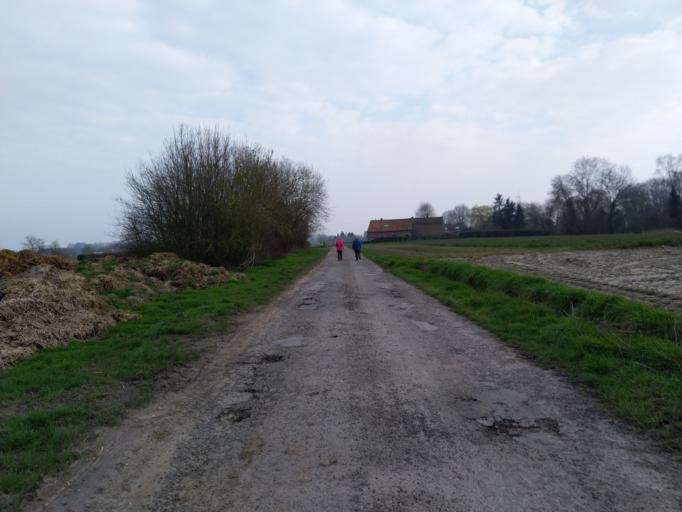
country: BE
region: Wallonia
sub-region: Province du Hainaut
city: Mons
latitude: 50.5221
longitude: 3.9995
